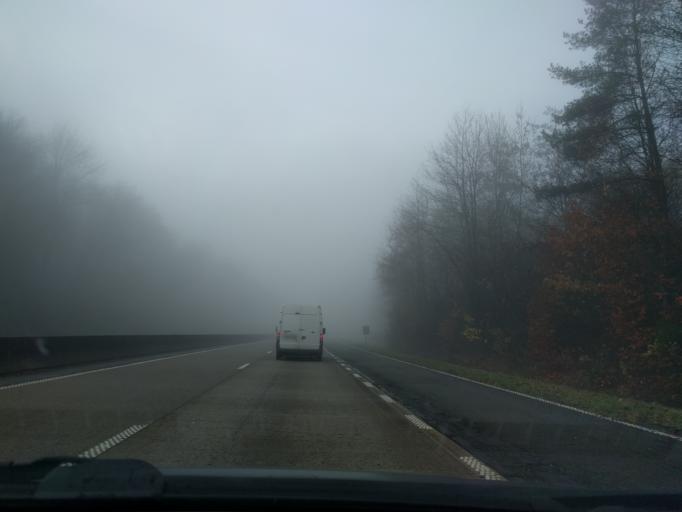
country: BE
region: Wallonia
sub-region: Province de Namur
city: Dinant
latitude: 50.2384
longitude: 4.9324
